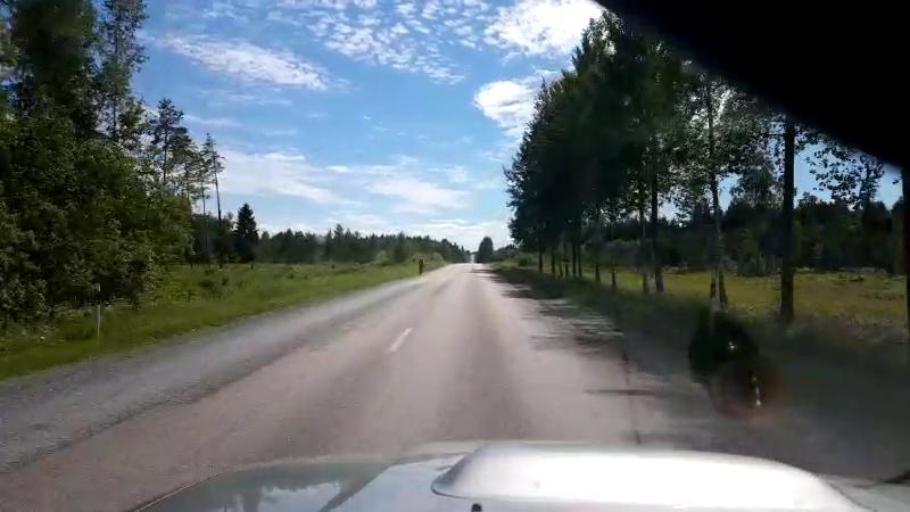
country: EE
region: Laeaene-Virumaa
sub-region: Rakke vald
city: Rakke
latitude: 58.8729
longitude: 26.2956
